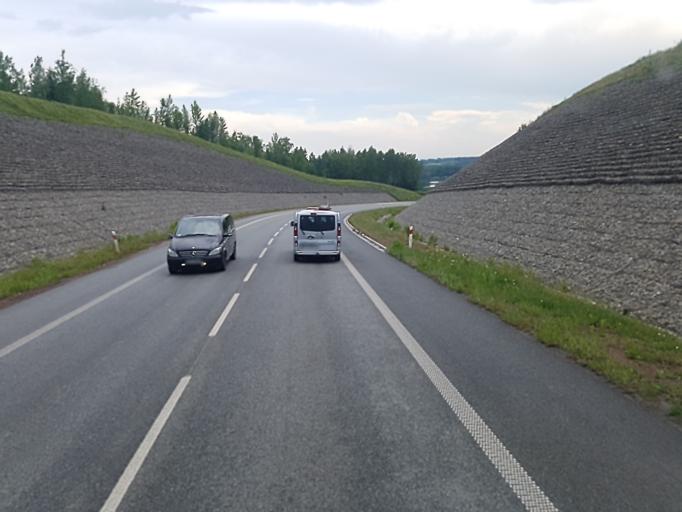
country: PL
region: Silesian Voivodeship
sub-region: Jastrzebie-Zdroj
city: Jastrzebie Zdroj
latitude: 49.9665
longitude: 18.5570
